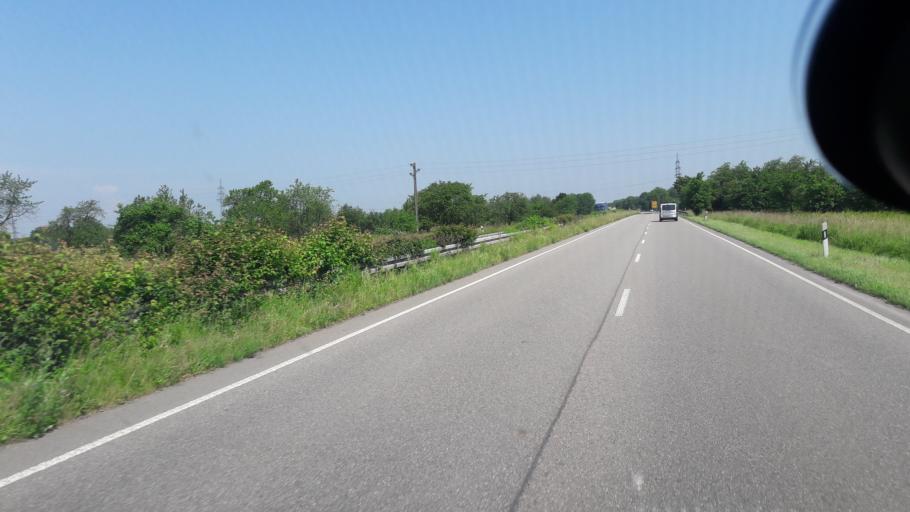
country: DE
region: Baden-Wuerttemberg
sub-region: Karlsruhe Region
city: Bischweier
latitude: 48.8446
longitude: 8.2679
